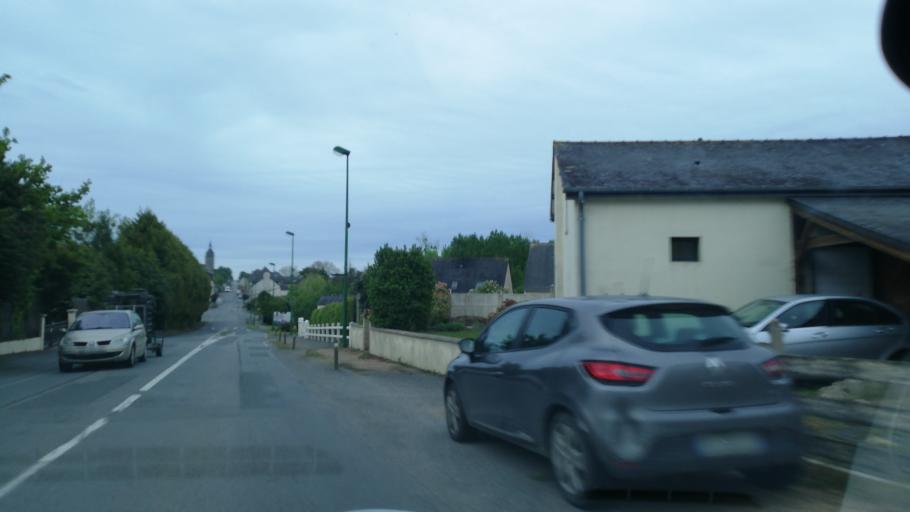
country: FR
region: Brittany
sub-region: Departement d'Ille-et-Vilaine
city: Irodouer
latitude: 48.2536
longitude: -1.9510
